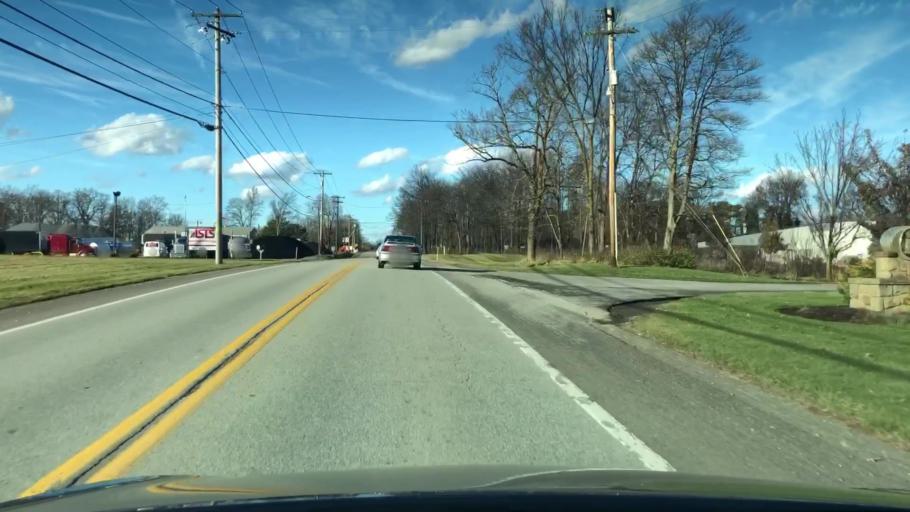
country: US
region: Pennsylvania
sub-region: Butler County
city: Saxonburg
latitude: 40.7338
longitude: -79.7605
